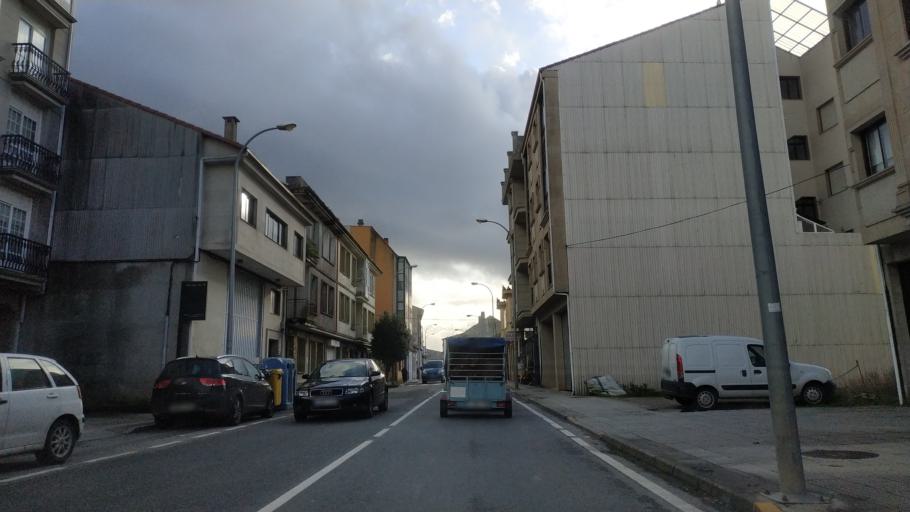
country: ES
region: Galicia
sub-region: Provincia da Coruna
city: Arzua
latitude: 42.9305
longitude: -8.1629
